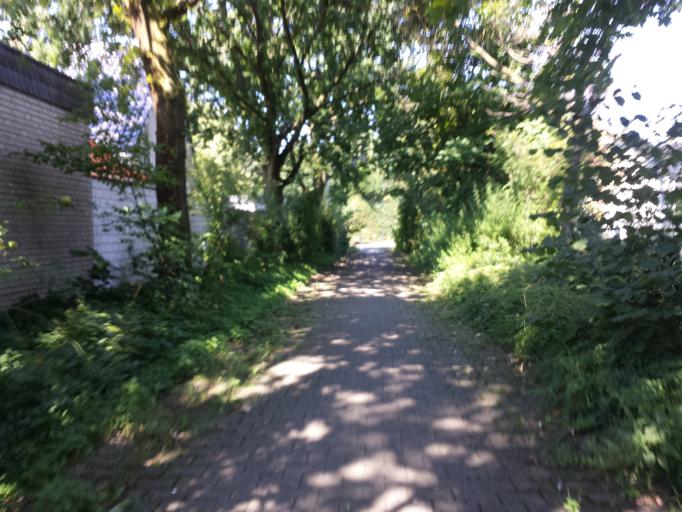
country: DE
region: North Rhine-Westphalia
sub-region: Regierungsbezirk Detmold
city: Guetersloh
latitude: 51.8824
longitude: 8.3786
